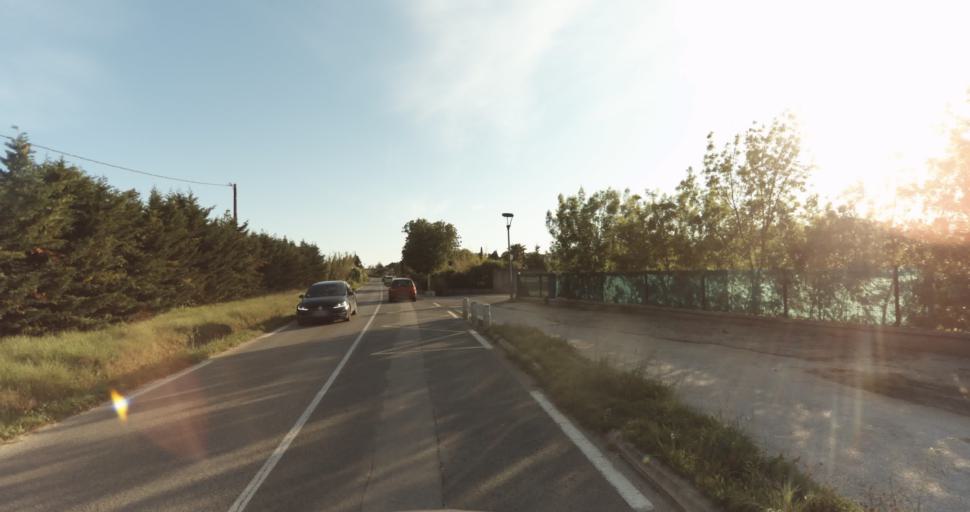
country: FR
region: Provence-Alpes-Cote d'Azur
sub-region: Departement du Var
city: La Crau
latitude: 43.1637
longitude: 6.1021
